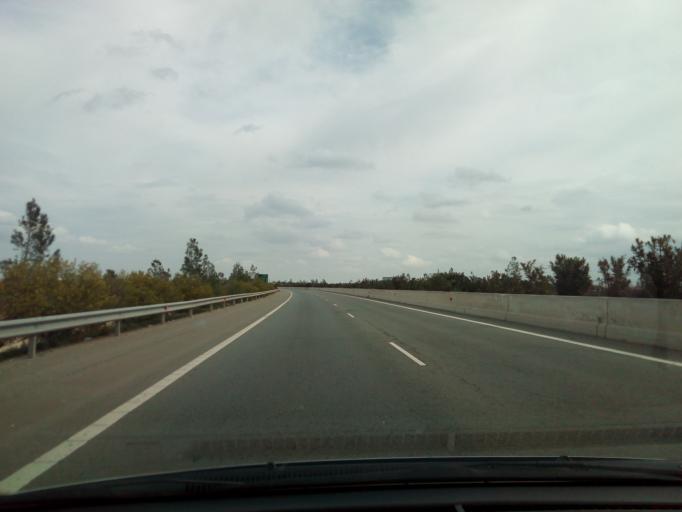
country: CY
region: Lefkosia
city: Kokkinotrimithia
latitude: 35.1600
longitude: 33.1884
